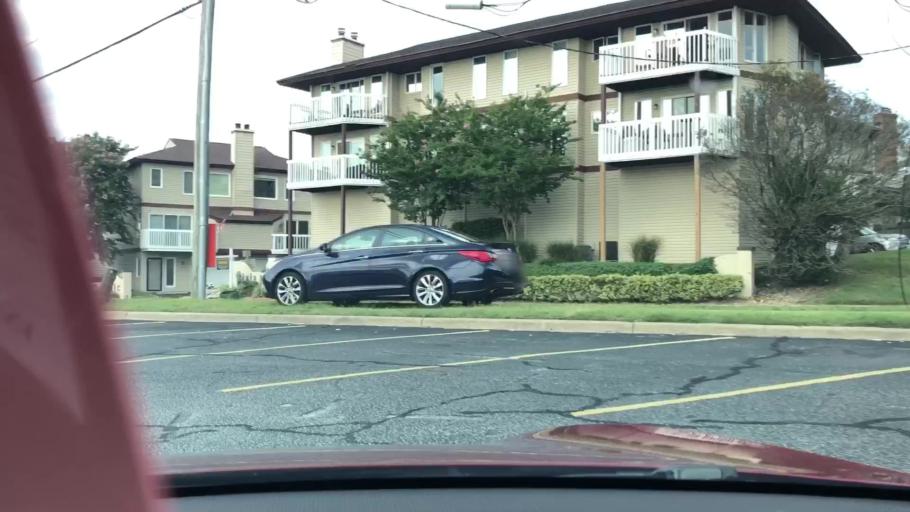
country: US
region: Virginia
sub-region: City of Virginia Beach
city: Virginia Beach
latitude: 36.9061
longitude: -76.0862
